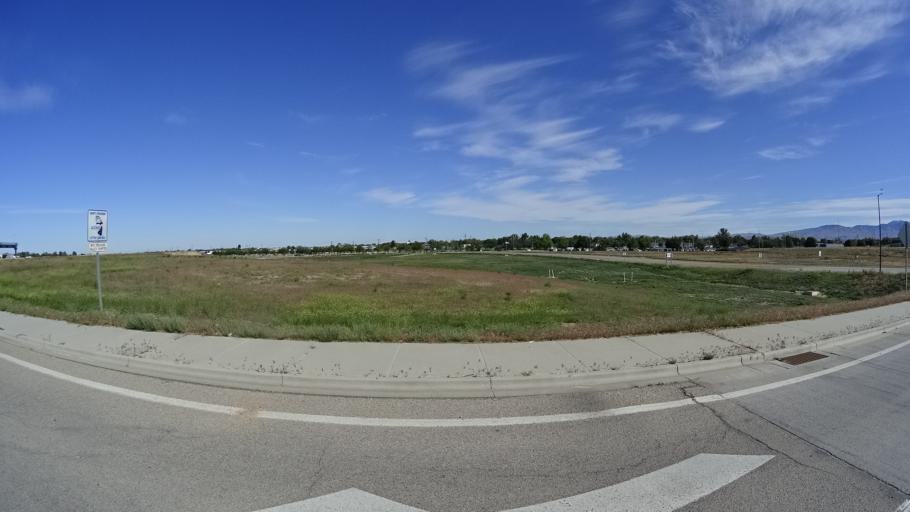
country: US
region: Idaho
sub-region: Ada County
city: Garden City
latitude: 43.5729
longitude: -116.2465
